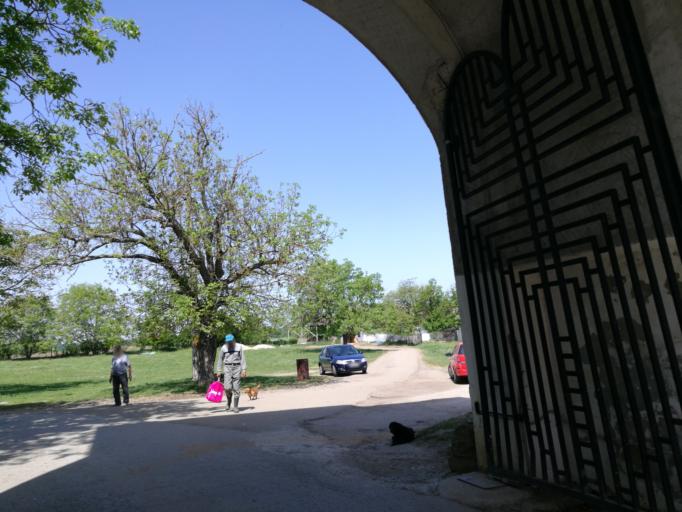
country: RO
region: Ilfov
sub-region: Comuna Gradistea
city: Gradistea
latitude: 44.6776
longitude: 26.2644
